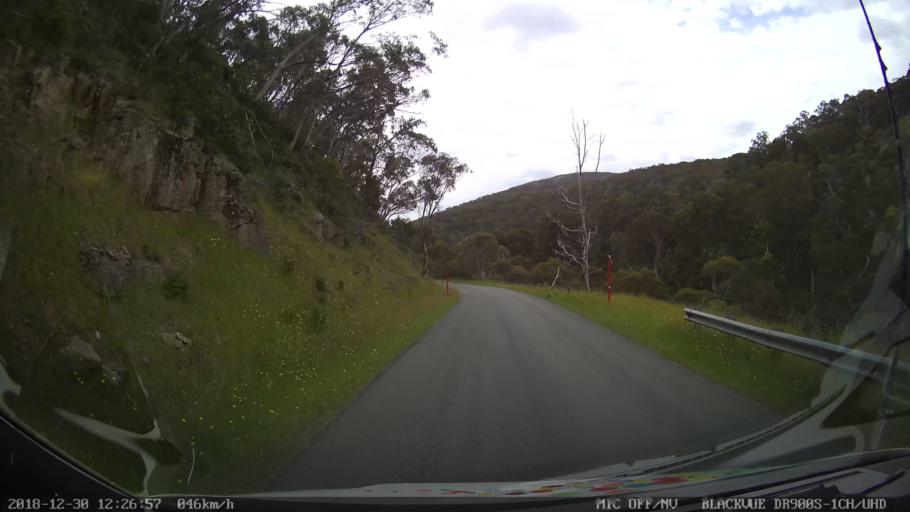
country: AU
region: New South Wales
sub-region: Snowy River
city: Jindabyne
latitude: -36.3345
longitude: 148.4899
